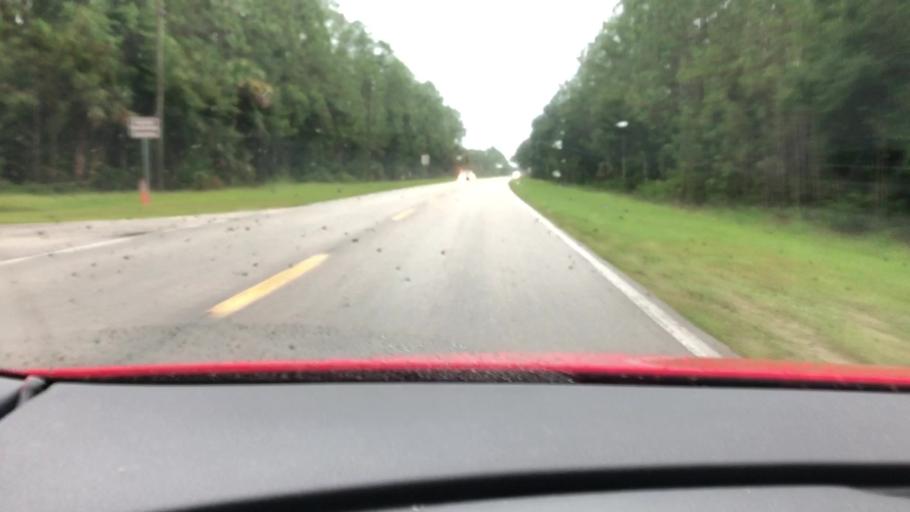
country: US
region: Florida
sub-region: Volusia County
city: Samsula-Spruce Creek
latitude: 29.0402
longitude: -81.0779
